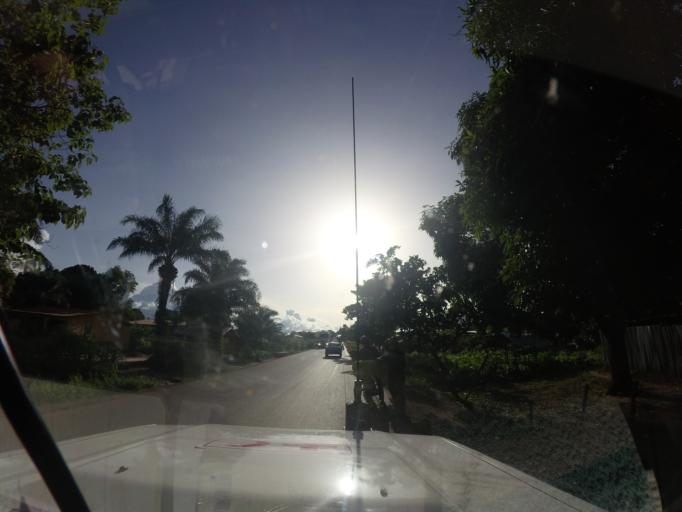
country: GN
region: Kindia
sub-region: Kindia
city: Kindia
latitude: 10.0202
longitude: -12.8328
